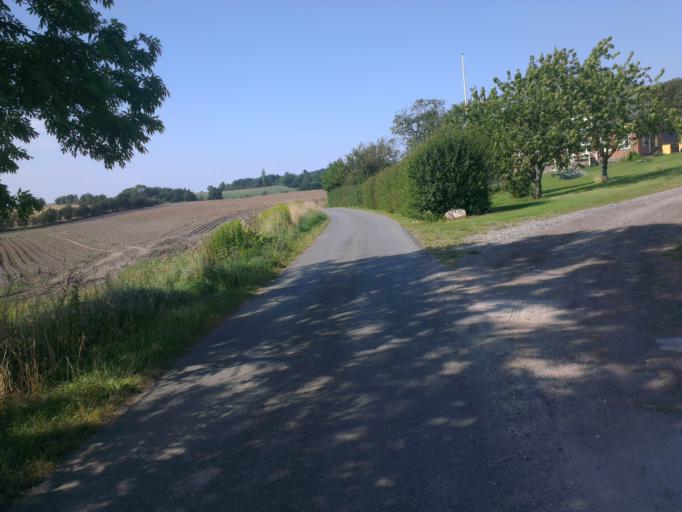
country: DK
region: Capital Region
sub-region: Frederikssund Kommune
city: Skibby
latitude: 55.7558
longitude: 11.9450
